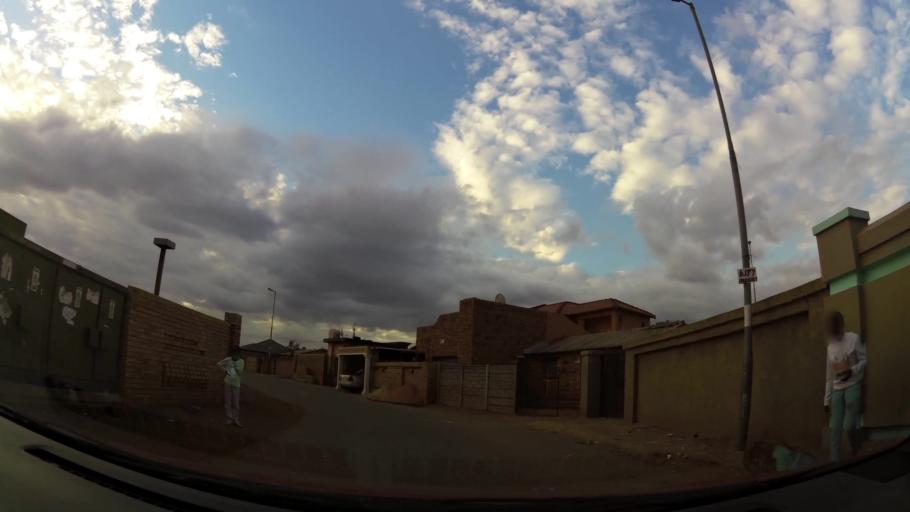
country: ZA
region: Gauteng
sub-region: City of Johannesburg Metropolitan Municipality
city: Soweto
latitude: -26.2460
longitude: 27.8310
